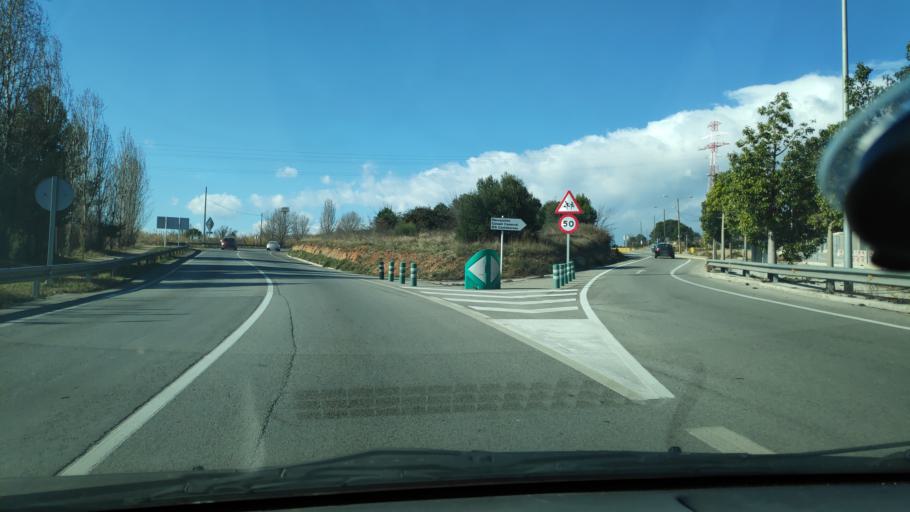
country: ES
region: Catalonia
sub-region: Provincia de Barcelona
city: Sant Quirze del Valles
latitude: 41.5531
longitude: 2.0670
